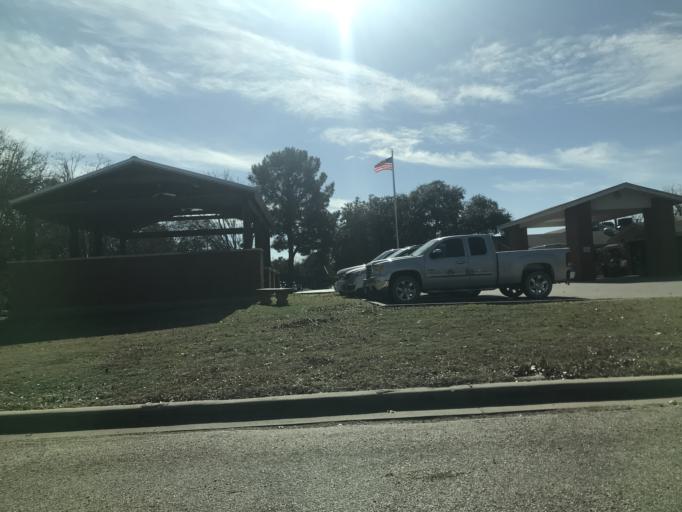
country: US
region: Texas
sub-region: Taylor County
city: Abilene
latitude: 32.4120
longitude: -99.7677
